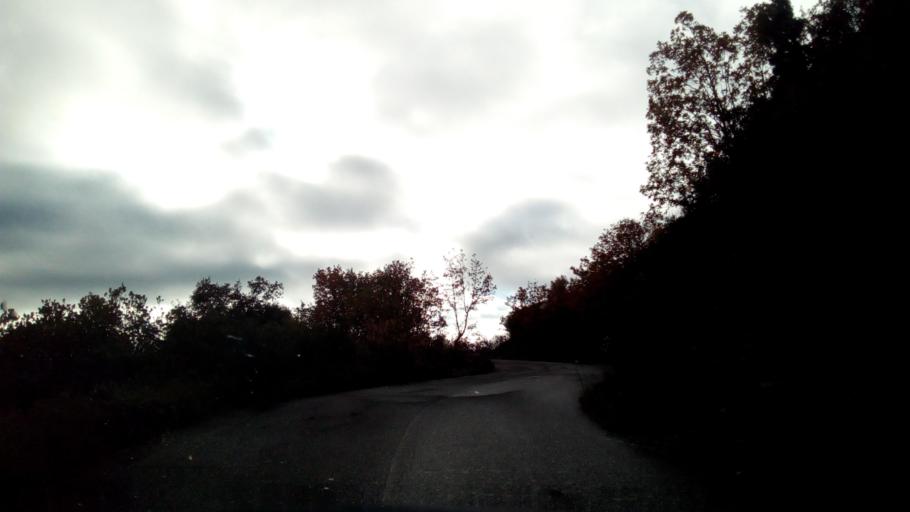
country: GR
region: West Greece
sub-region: Nomos Aitolias kai Akarnanias
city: Nafpaktos
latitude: 38.5209
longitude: 21.9715
